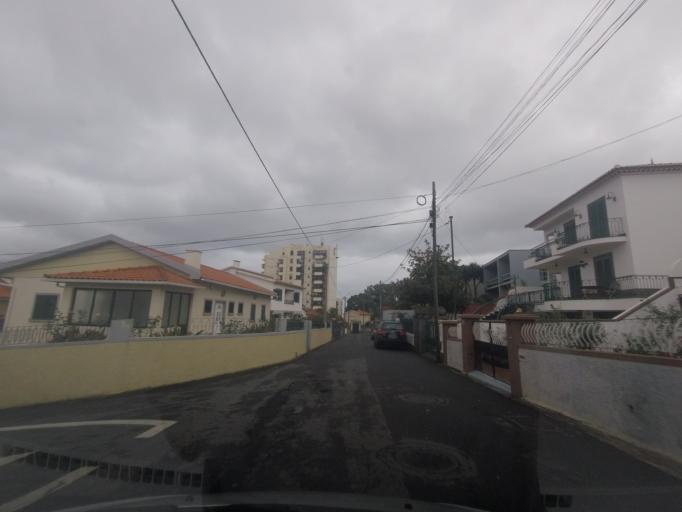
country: PT
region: Madeira
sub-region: Funchal
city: Nossa Senhora do Monte
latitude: 32.6512
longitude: -16.9337
